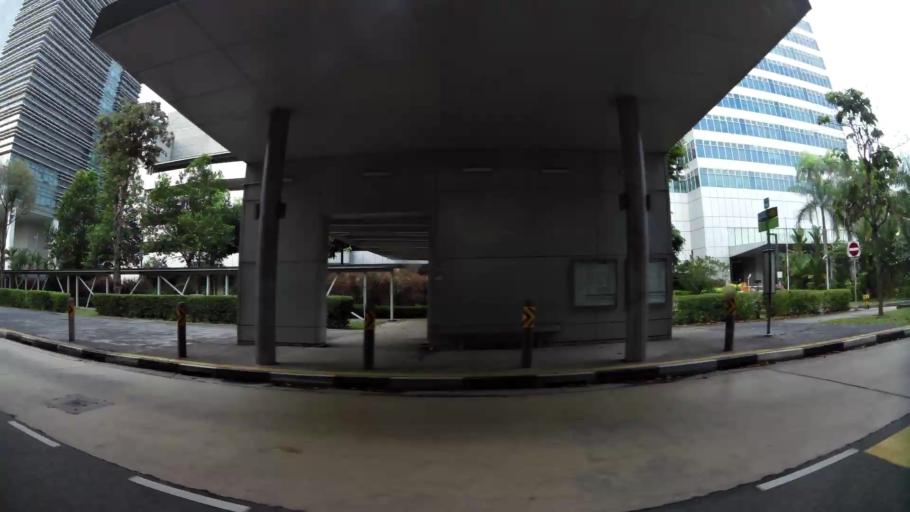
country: SG
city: Singapore
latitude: 1.2736
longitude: 103.8008
